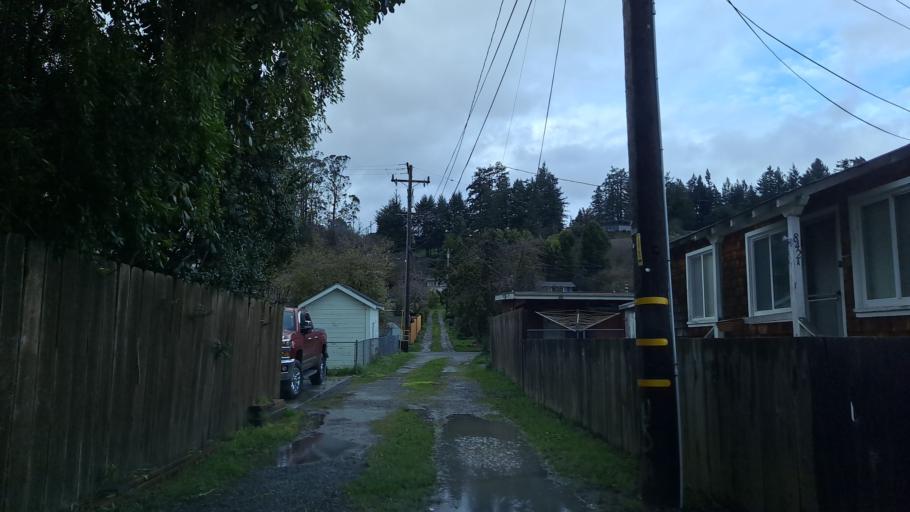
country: US
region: California
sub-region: Humboldt County
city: Fortuna
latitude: 40.5993
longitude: -124.1550
